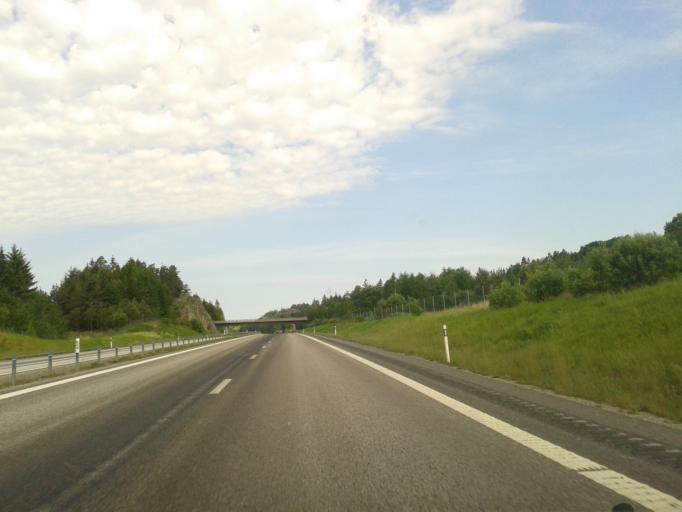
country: SE
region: Vaestra Goetaland
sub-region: Lysekils Kommun
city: Brastad
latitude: 58.5472
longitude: 11.5134
